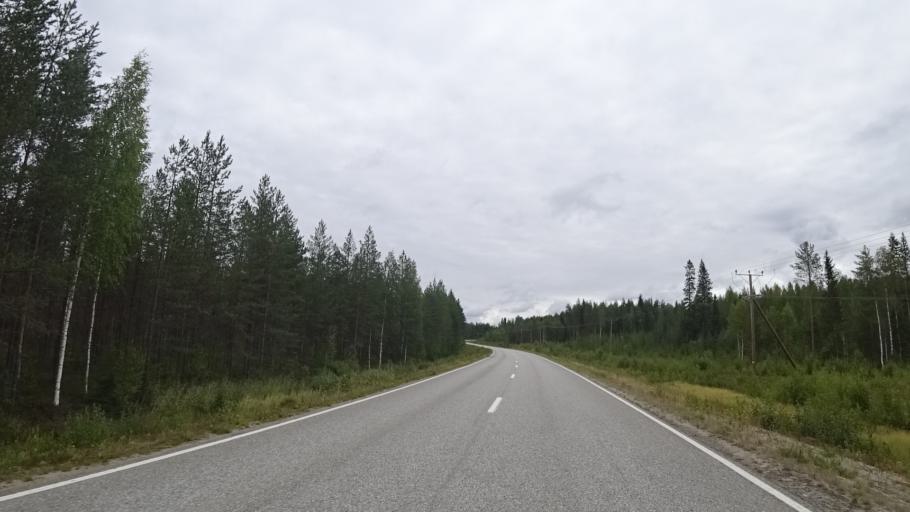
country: FI
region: North Karelia
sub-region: Joensuu
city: Ilomantsi
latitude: 62.6210
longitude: 31.2330
